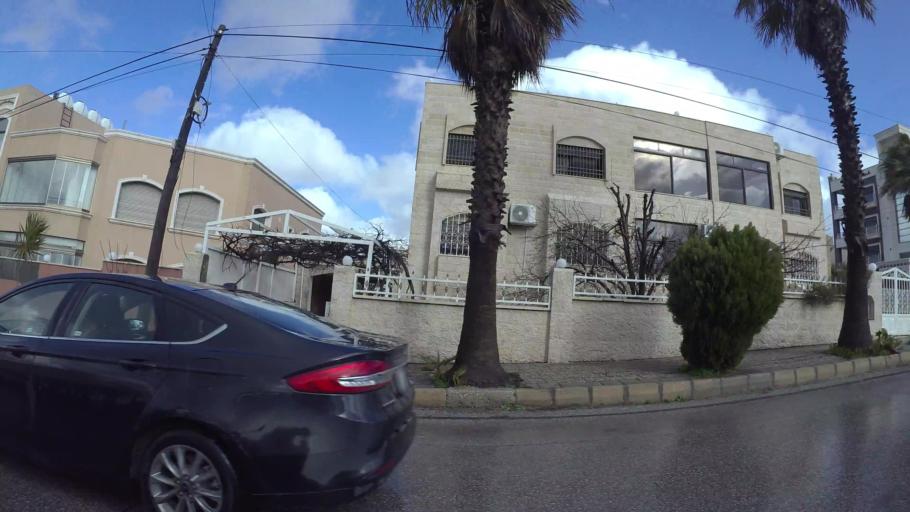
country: JO
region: Amman
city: Al Jubayhah
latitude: 32.0308
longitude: 35.8640
